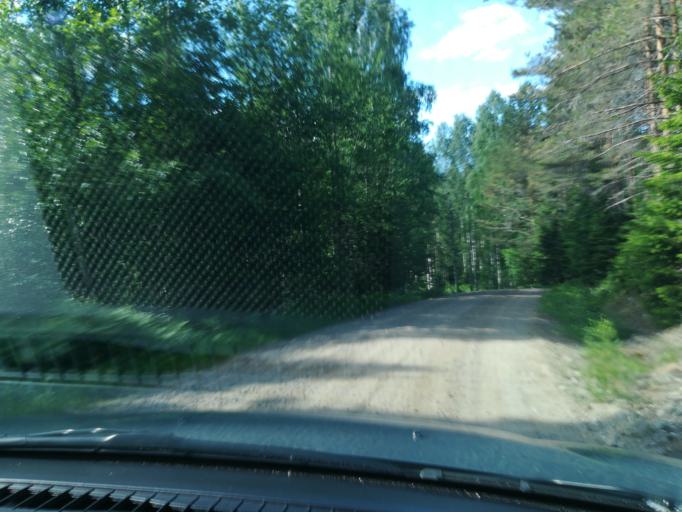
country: FI
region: Southern Savonia
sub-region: Mikkeli
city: Puumala
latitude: 61.6532
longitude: 28.1719
